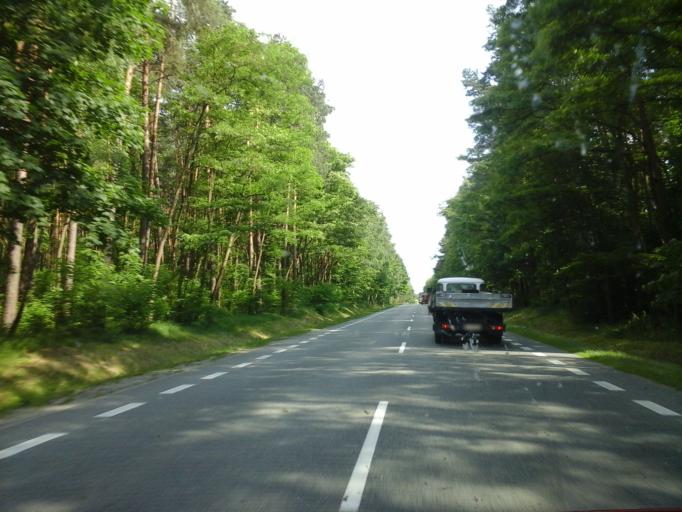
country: PL
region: Swietokrzyskie
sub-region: Powiat konecki
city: Ruda Maleniecka
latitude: 51.1521
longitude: 20.2370
